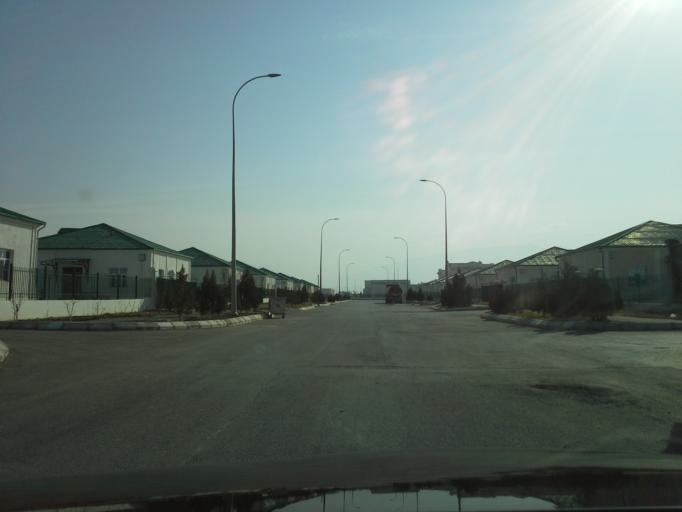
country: TM
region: Ahal
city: Abadan
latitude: 38.1737
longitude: 58.0489
